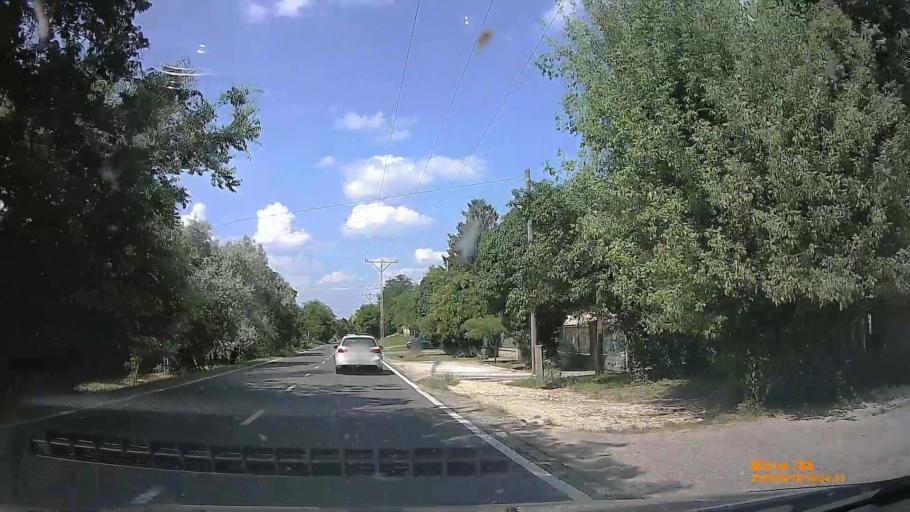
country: HU
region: Budapest
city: Budapest XVII. keruelet
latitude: 47.4612
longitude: 19.2464
